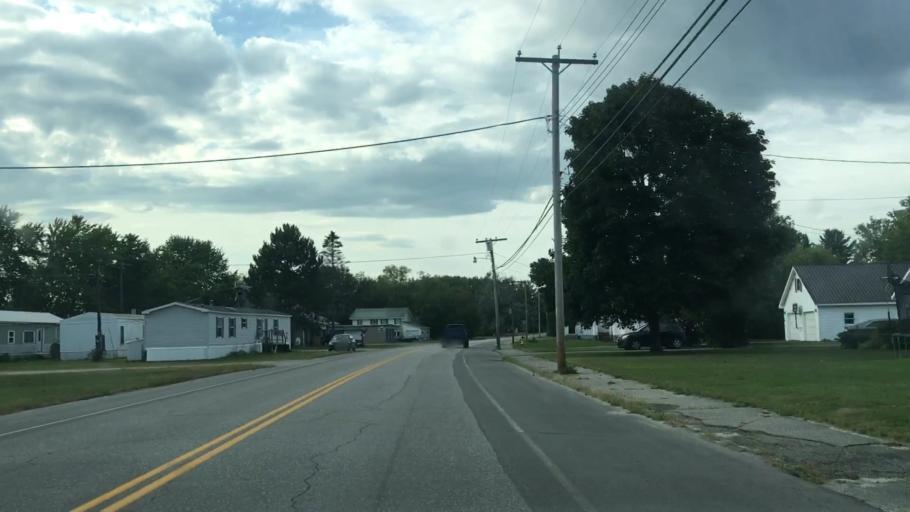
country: US
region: Maine
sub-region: Penobscot County
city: Howland
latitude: 45.2431
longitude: -68.6607
